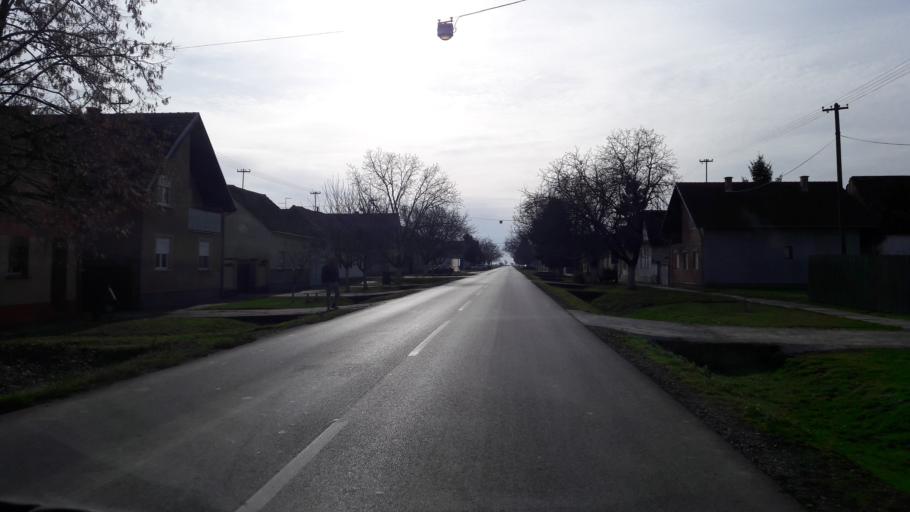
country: HR
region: Osjecko-Baranjska
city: Semeljci
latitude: 45.3477
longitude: 18.5575
